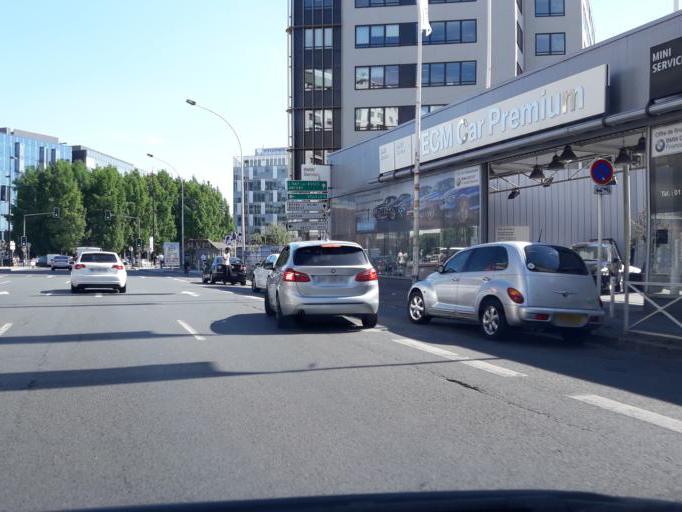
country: FR
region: Ile-de-France
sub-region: Departement du Val-de-Marne
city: Arcueil
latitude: 48.8113
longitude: 2.3264
